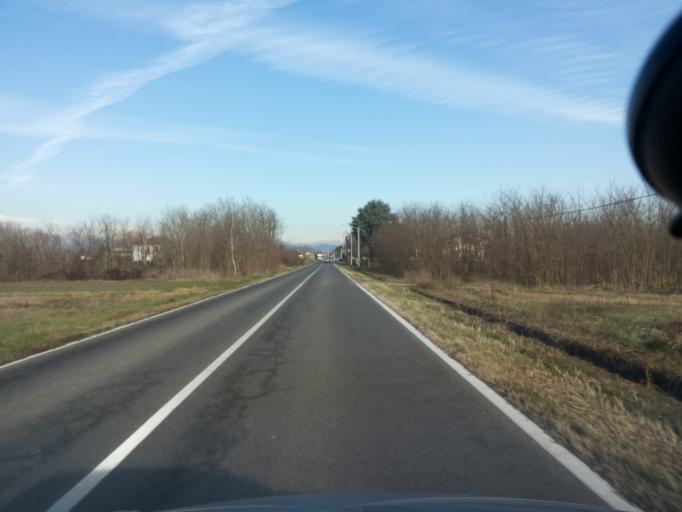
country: IT
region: Piedmont
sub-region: Provincia di Vercelli
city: Ghislarengo
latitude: 45.5191
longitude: 8.3868
